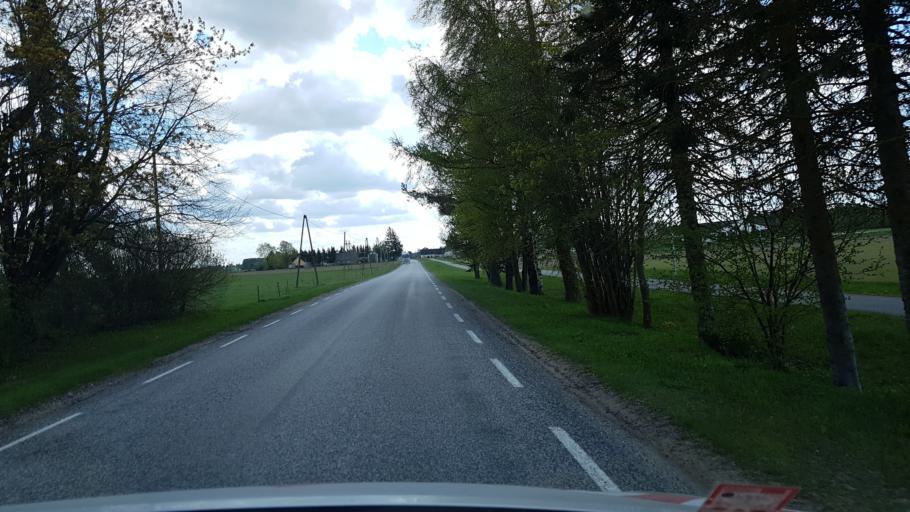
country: EE
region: Jogevamaa
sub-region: Poltsamaa linn
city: Poltsamaa
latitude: 58.6798
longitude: 25.9546
